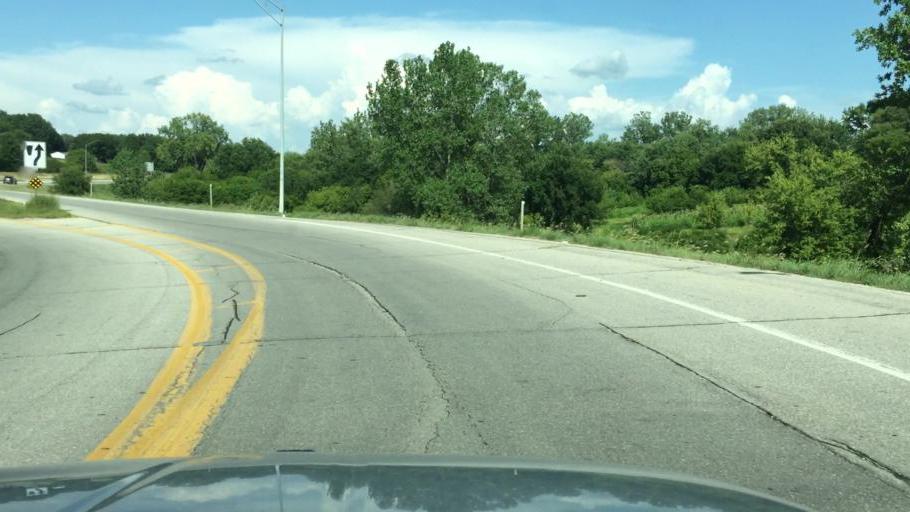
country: US
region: Iowa
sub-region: Jasper County
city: Newton
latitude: 41.6826
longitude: -93.0754
